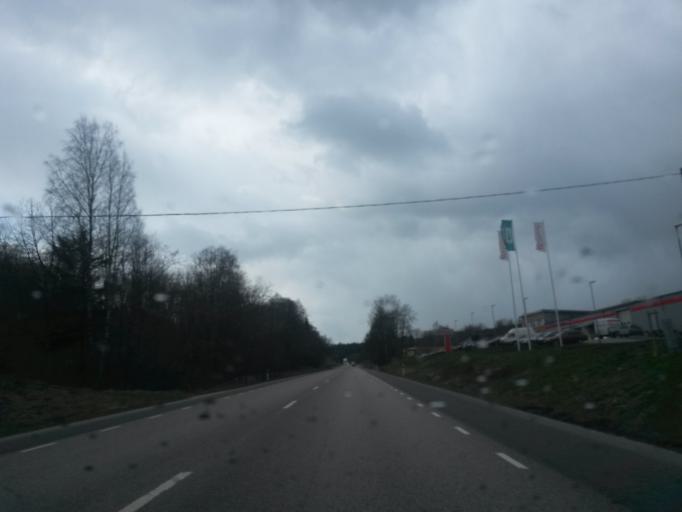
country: SE
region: Vaestra Goetaland
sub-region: Skovde Kommun
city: Skoevde
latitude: 58.3870
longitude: 13.7974
